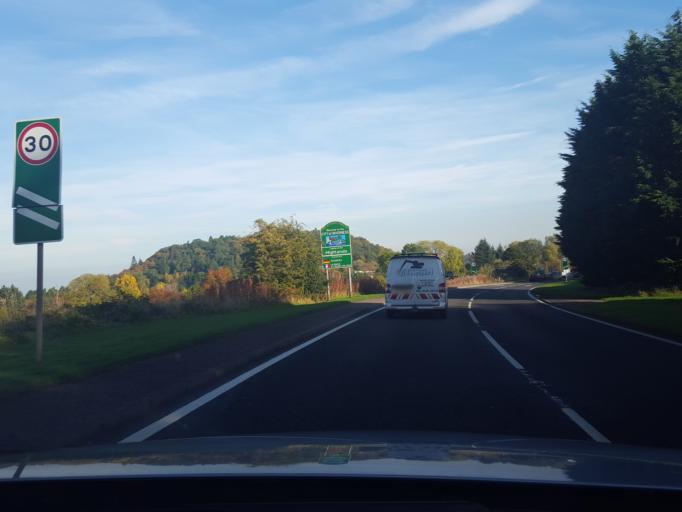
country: GB
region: Scotland
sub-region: Highland
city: Inverness
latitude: 57.4630
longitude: -4.2542
